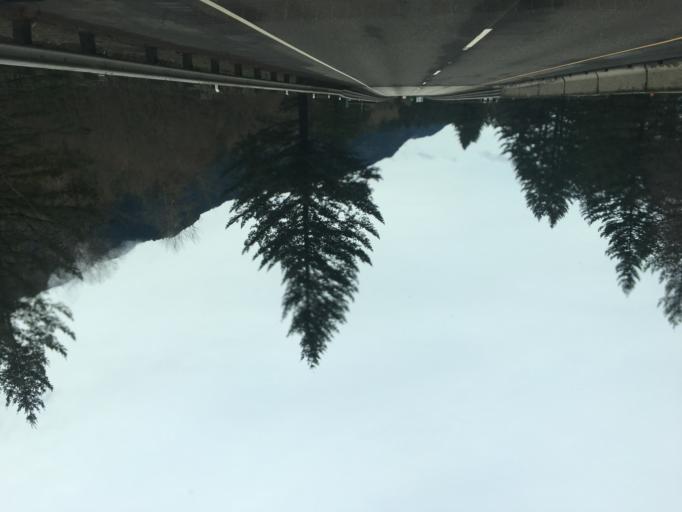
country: US
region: Oregon
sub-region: Hood River County
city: Cascade Locks
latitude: 45.6002
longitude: -122.0492
